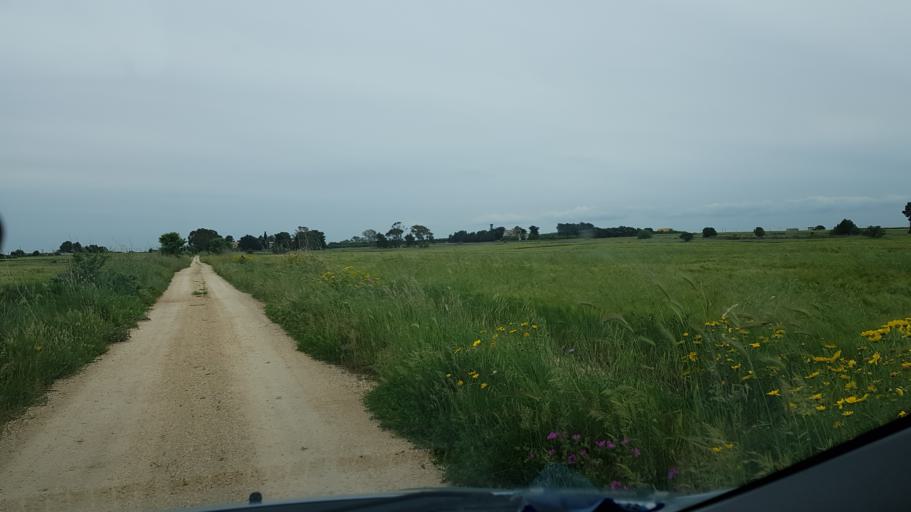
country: IT
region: Apulia
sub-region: Provincia di Brindisi
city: Brindisi
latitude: 40.6536
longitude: 17.8821
